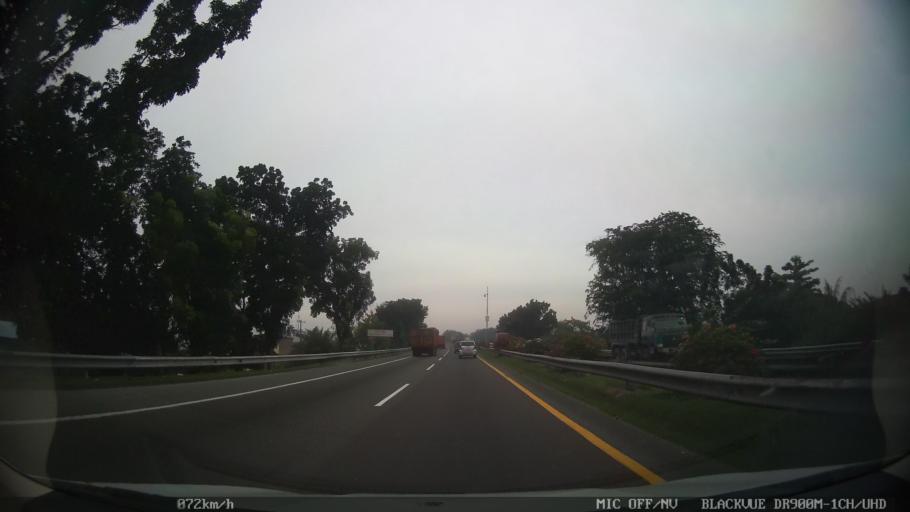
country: ID
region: North Sumatra
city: Medan
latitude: 3.5868
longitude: 98.7241
